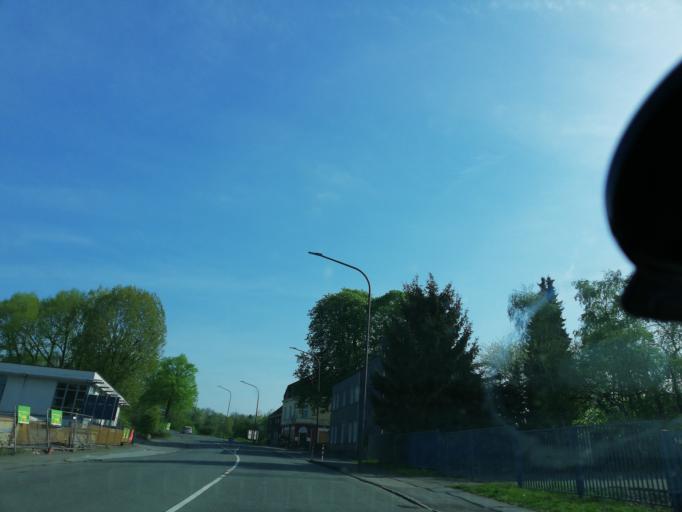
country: DE
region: North Rhine-Westphalia
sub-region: Regierungsbezirk Arnsberg
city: Schwelm
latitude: 51.2997
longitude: 7.2502
